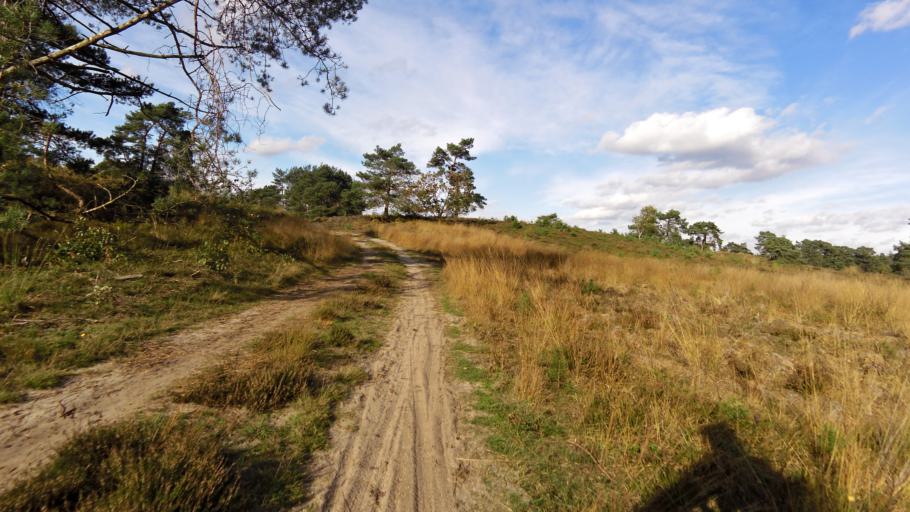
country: NL
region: Gelderland
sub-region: Gemeente Epe
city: Emst
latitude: 52.3392
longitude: 5.8832
